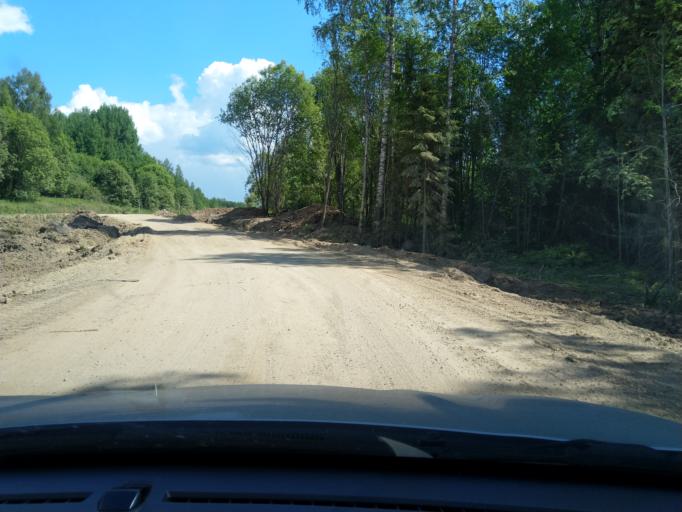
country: RU
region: Perm
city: Pozhva
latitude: 59.4194
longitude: 56.2492
